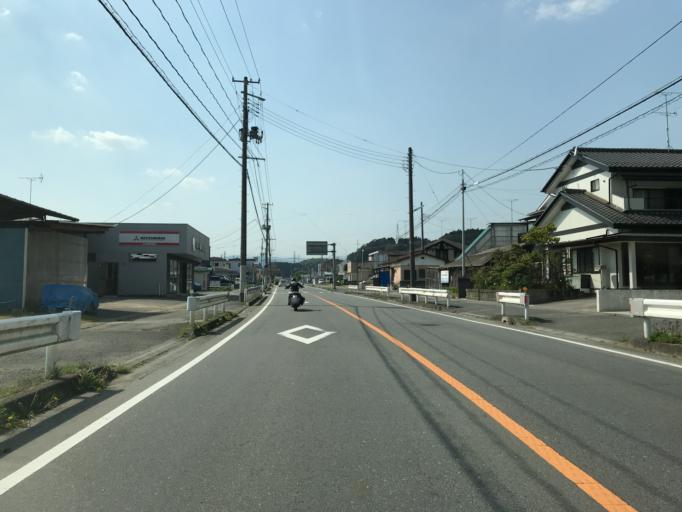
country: JP
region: Ibaraki
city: Kitaibaraki
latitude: 36.9243
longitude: 140.7834
